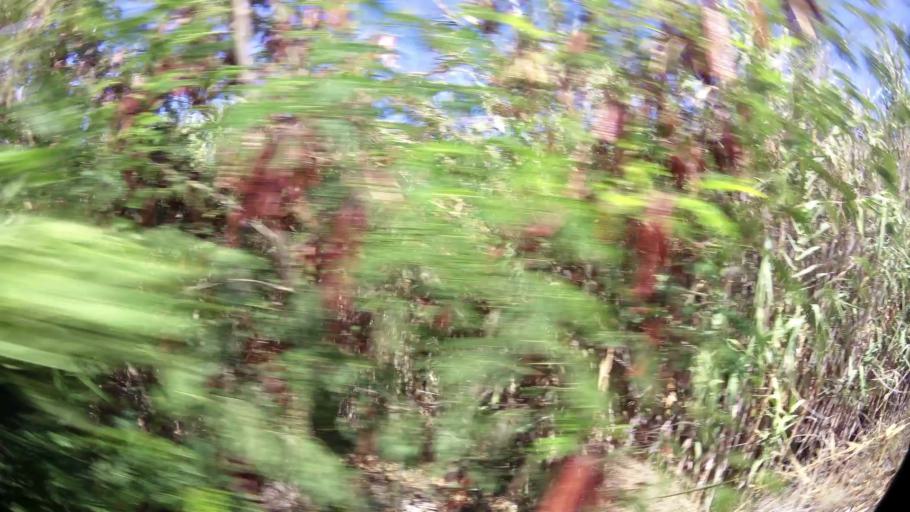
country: CY
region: Larnaka
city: Livadia
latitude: 34.9551
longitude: 33.6353
